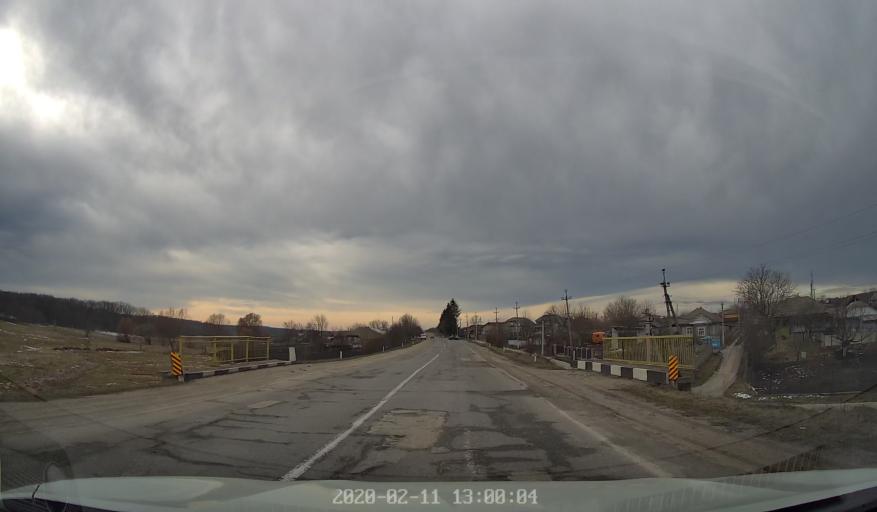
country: MD
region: Briceni
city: Briceni
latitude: 48.3264
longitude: 27.0232
